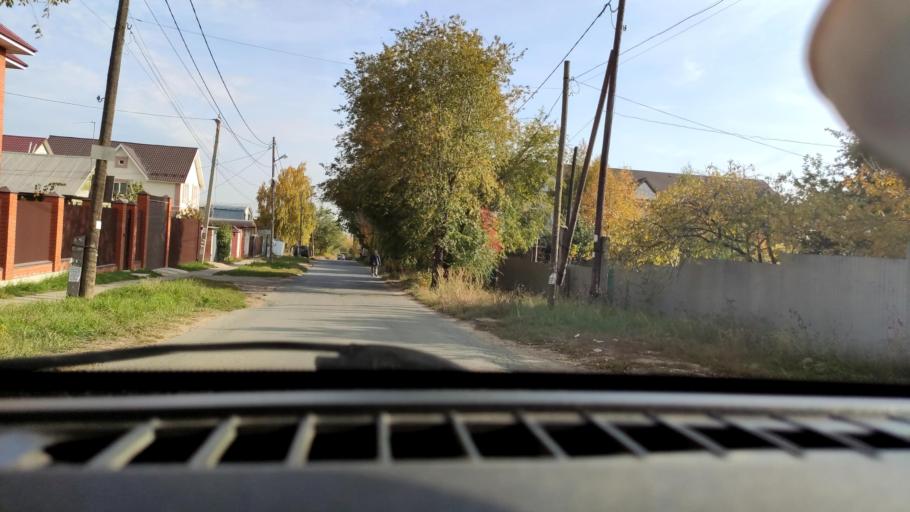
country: RU
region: Samara
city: Samara
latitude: 53.1856
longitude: 50.2039
